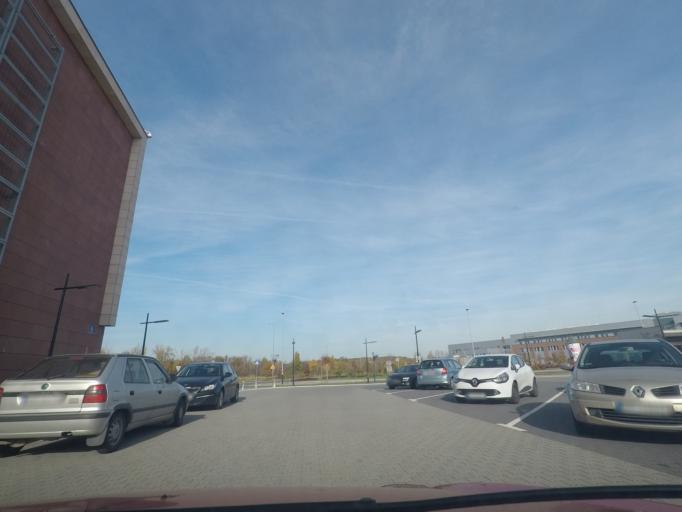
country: PL
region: Lesser Poland Voivodeship
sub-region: Krakow
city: Krakow
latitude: 50.0275
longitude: 19.9029
